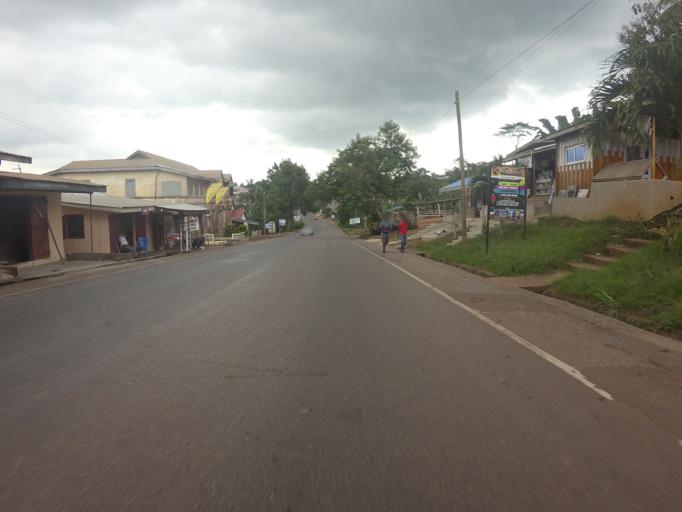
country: GH
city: Akropong
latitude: 5.9383
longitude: -0.1168
